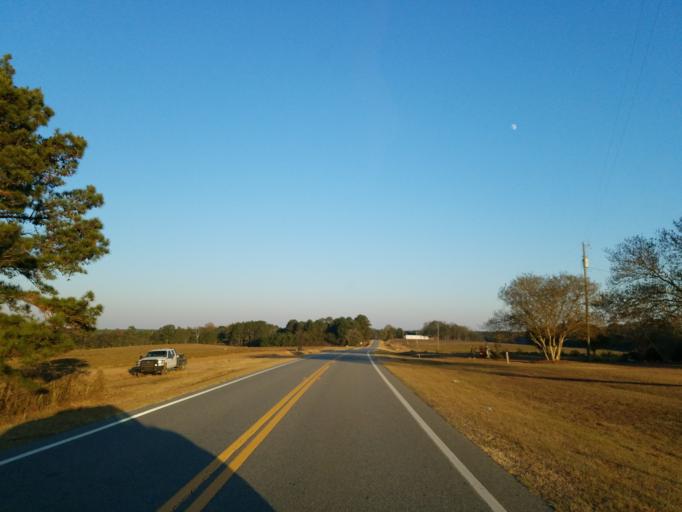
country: US
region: Georgia
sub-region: Wilcox County
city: Rochelle
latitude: 31.8159
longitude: -83.5178
